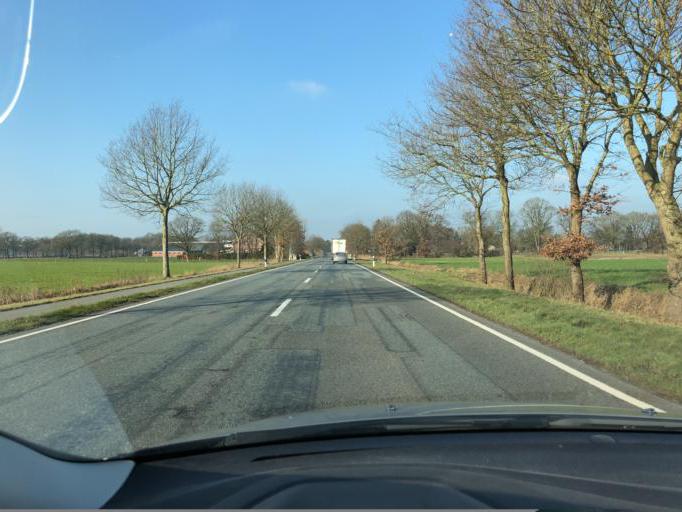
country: DE
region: Lower Saxony
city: Apen
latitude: 53.2974
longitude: 7.8152
